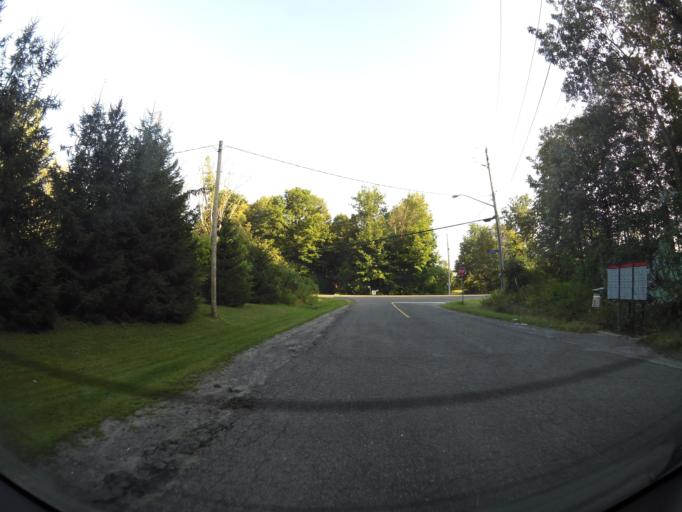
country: CA
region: Ontario
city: Clarence-Rockland
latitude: 45.4997
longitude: -75.4136
